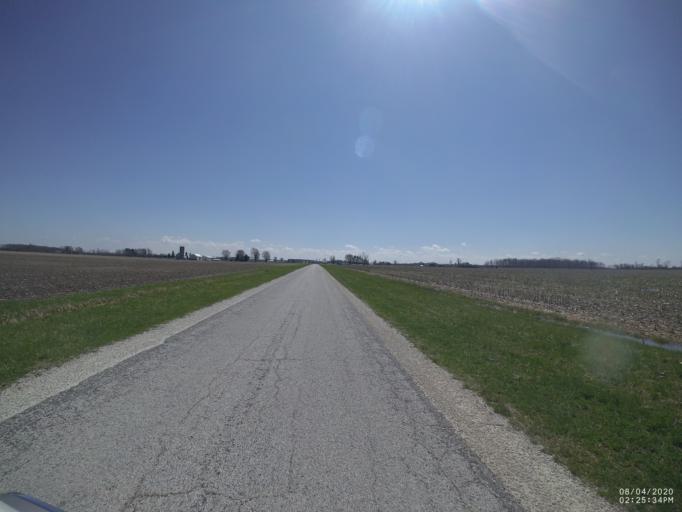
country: US
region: Ohio
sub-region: Sandusky County
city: Gibsonburg
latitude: 41.2963
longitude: -83.2595
